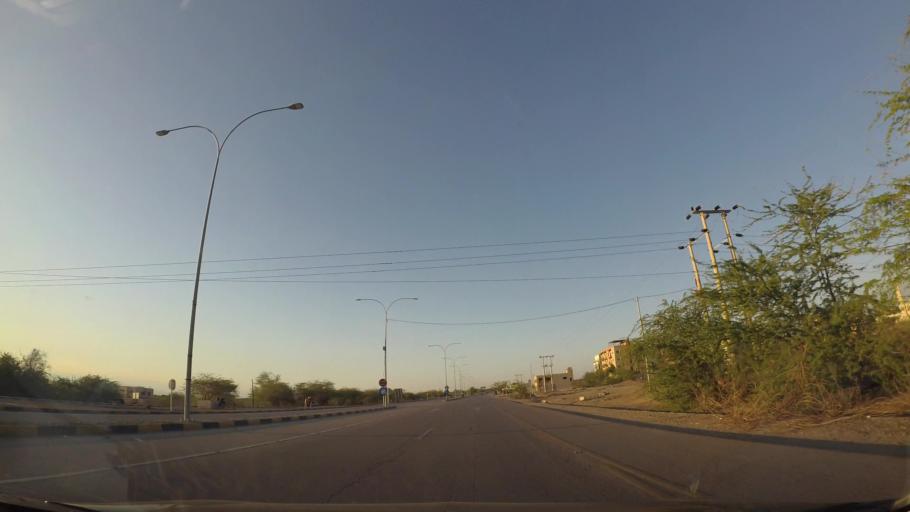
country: PS
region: West Bank
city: Jericho
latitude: 31.7602
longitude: 35.5931
